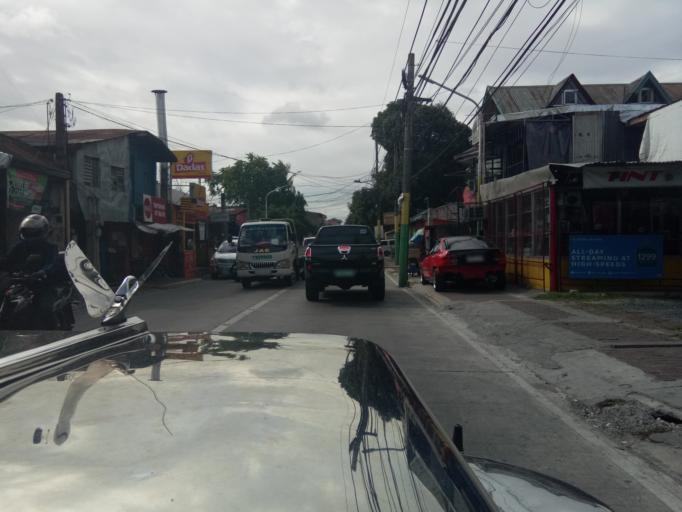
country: PH
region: Calabarzon
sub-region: Province of Cavite
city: Dasmarinas
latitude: 14.3197
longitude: 120.9406
